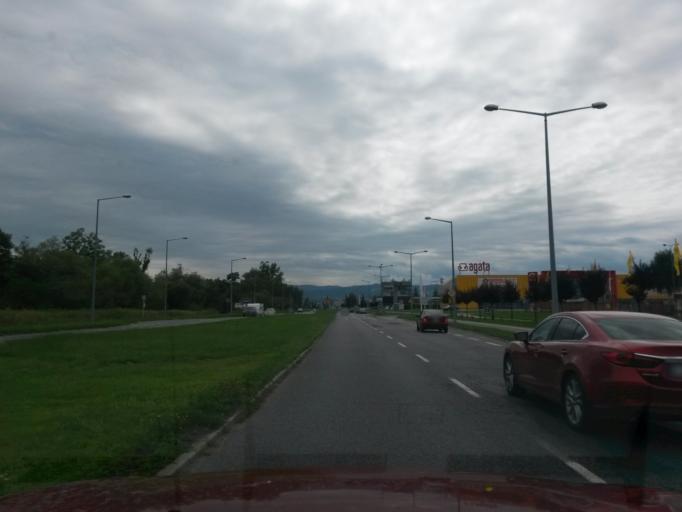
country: PL
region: Lesser Poland Voivodeship
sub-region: Powiat nowosadecki
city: Nowy Sacz
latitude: 49.6034
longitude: 20.7288
